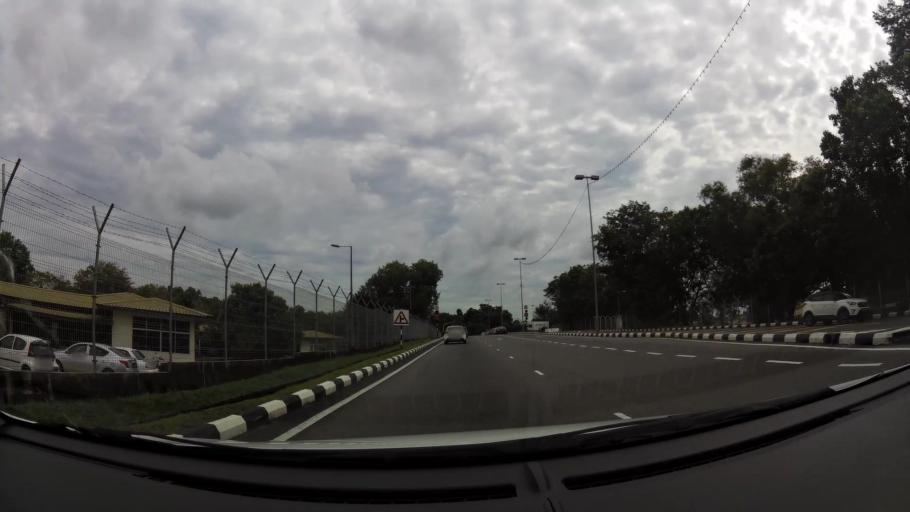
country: BN
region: Brunei and Muara
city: Bandar Seri Begawan
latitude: 4.9048
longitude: 114.9021
